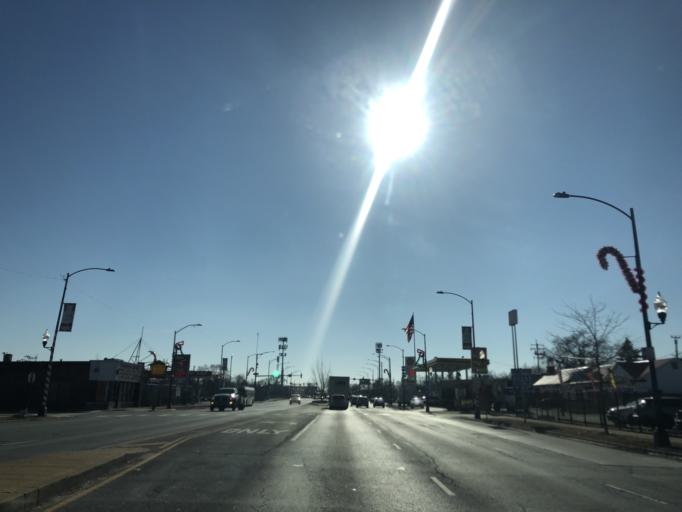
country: US
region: Illinois
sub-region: Cook County
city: Calumet Park
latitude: 41.7166
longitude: -87.6431
